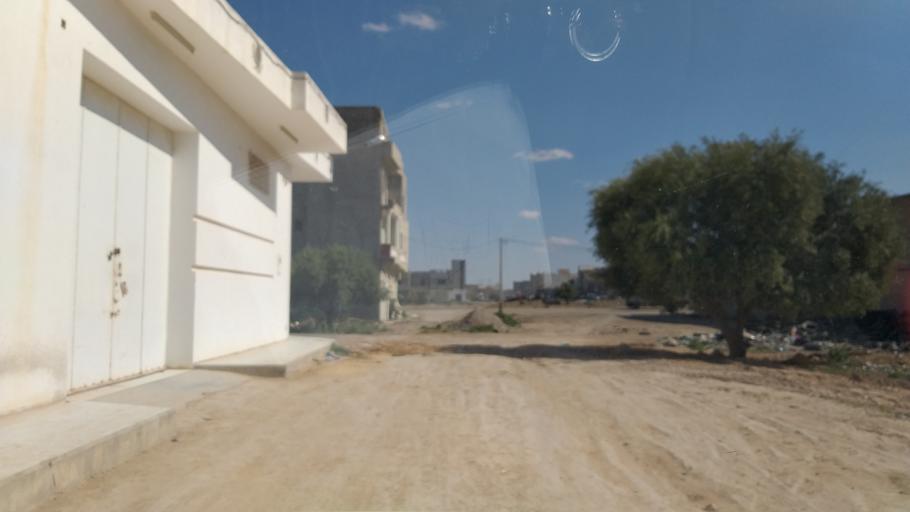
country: TN
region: Al Mahdiyah
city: El Jem
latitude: 35.2935
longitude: 10.6945
